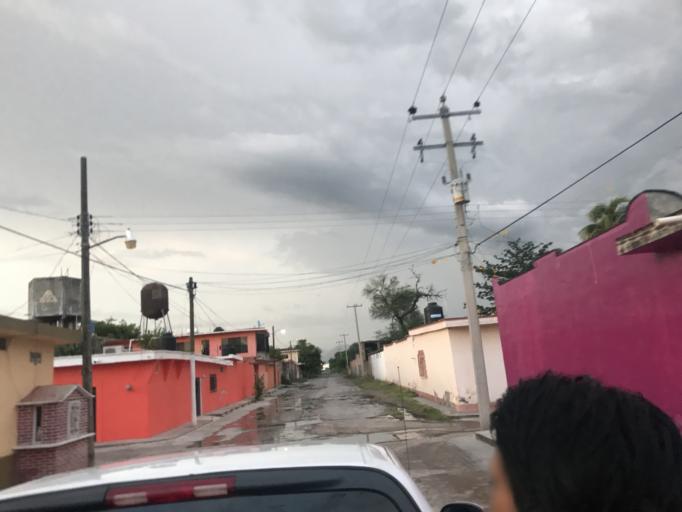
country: MX
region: Morelos
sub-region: Axochiapan
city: Quebrantadero
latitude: 18.5262
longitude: -98.7921
